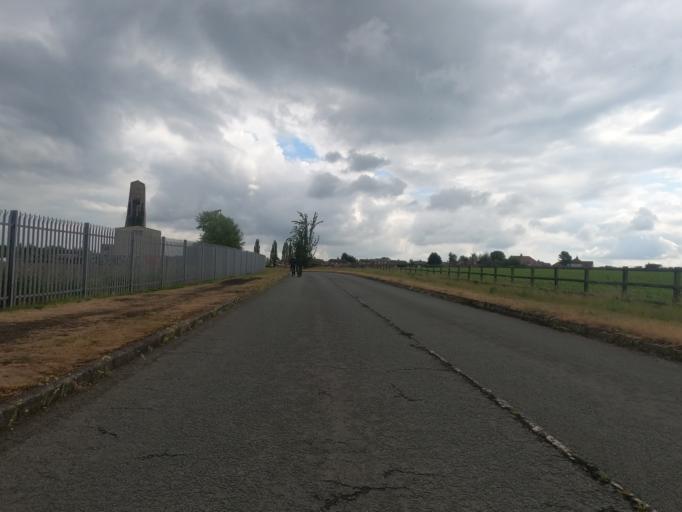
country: GB
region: England
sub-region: Cheshire West and Chester
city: Winsford
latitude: 53.2134
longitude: -2.5234
